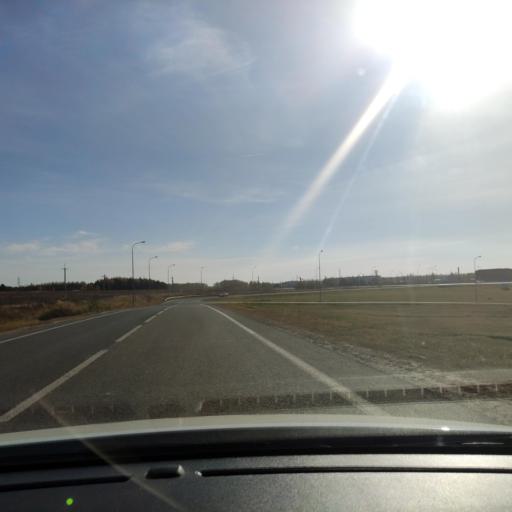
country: RU
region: Tatarstan
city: Vysokaya Gora
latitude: 55.7471
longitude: 49.4005
